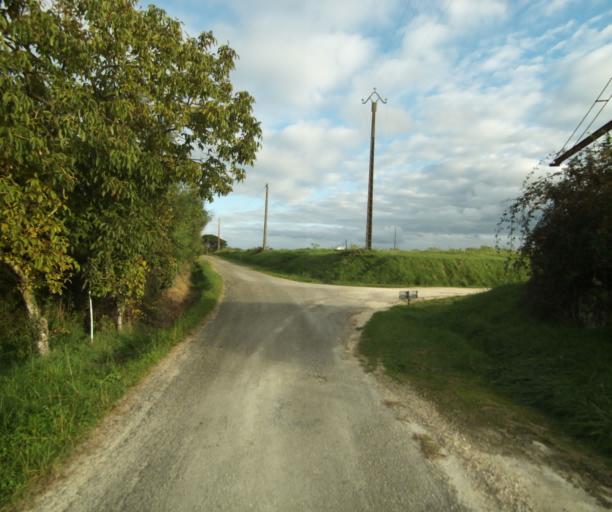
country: FR
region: Aquitaine
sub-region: Departement des Landes
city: Gabarret
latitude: 43.9442
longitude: 0.0787
